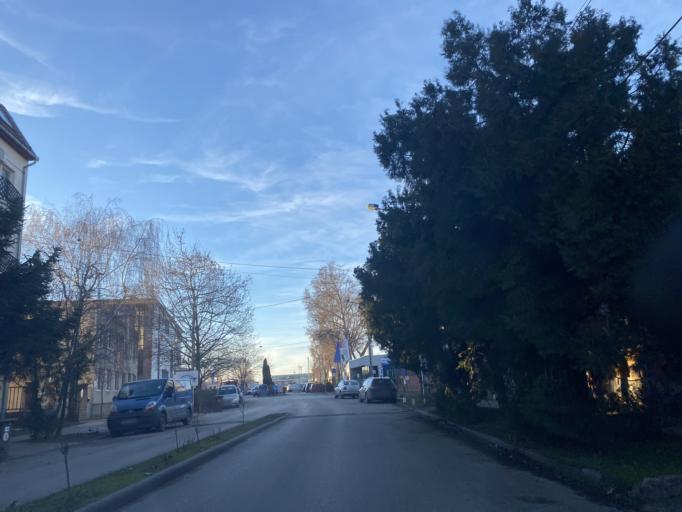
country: HU
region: Csongrad
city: Szeged
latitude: 46.2599
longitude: 20.1331
